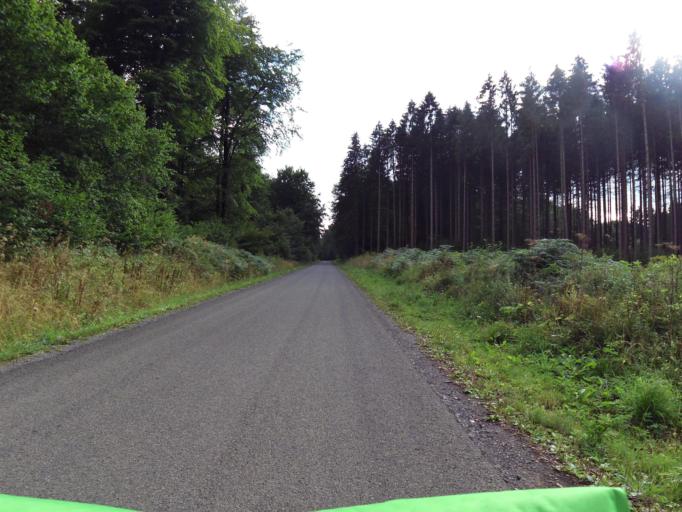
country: BE
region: Wallonia
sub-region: Province de Namur
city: Bievre
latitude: 49.9254
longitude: 5.0080
